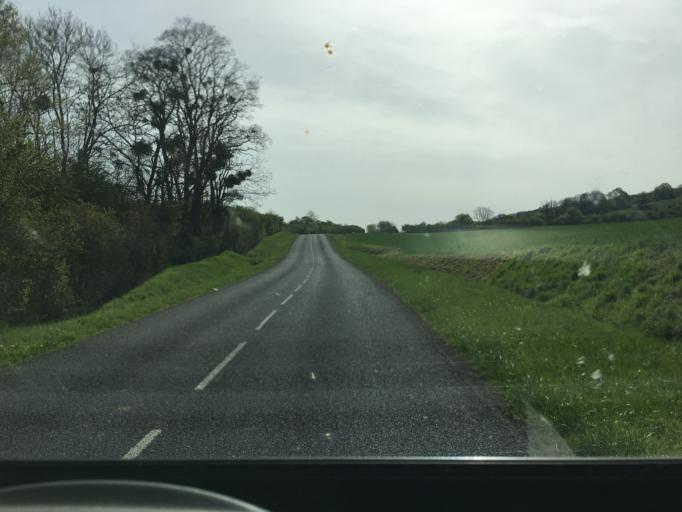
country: FR
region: Lorraine
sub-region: Departement de Meurthe-et-Moselle
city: Dommartin-les-Toul
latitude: 48.6711
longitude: 5.9322
